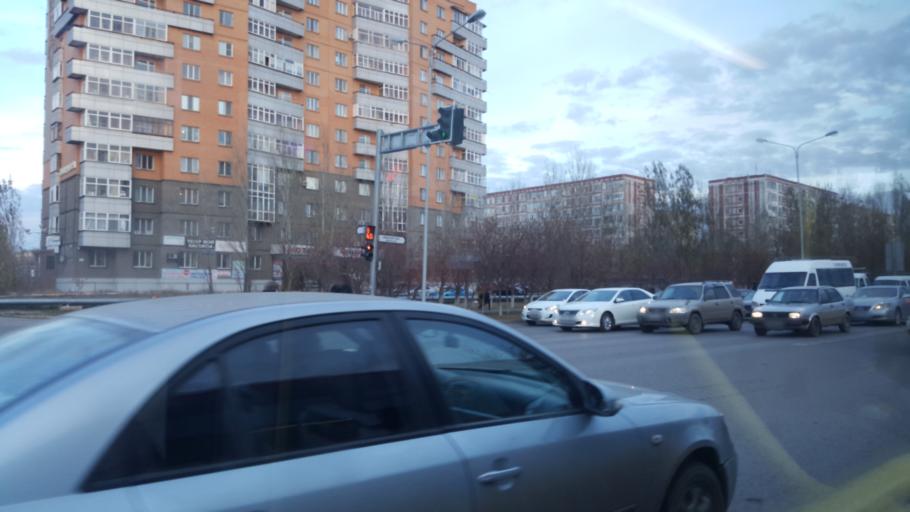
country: KZ
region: Astana Qalasy
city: Astana
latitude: 51.1543
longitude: 71.4863
